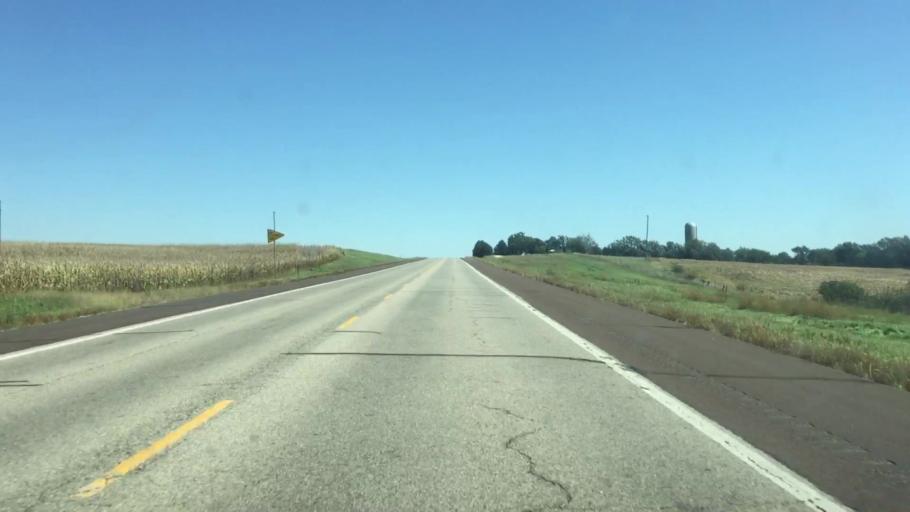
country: US
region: Kansas
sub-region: Nemaha County
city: Seneca
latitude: 39.8421
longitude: -96.3031
